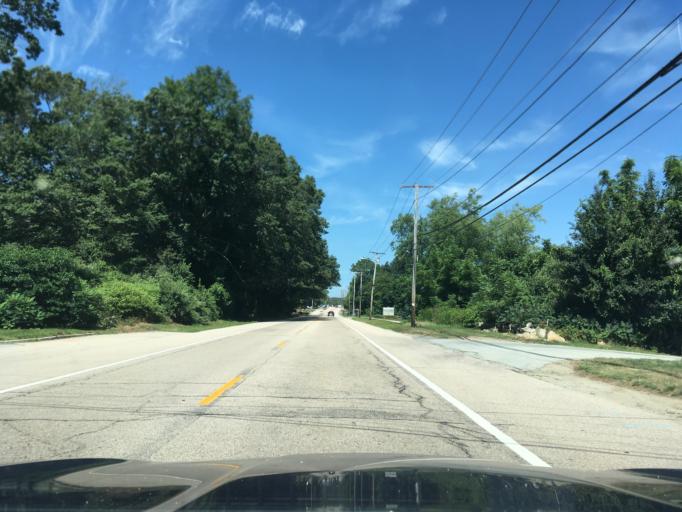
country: US
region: Rhode Island
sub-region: Kent County
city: East Greenwich
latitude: 41.6563
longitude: -71.4972
